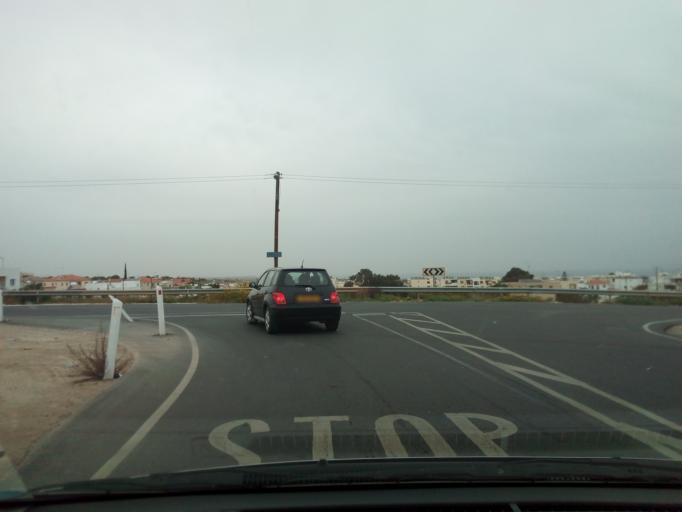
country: CY
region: Ammochostos
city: Paralimni
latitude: 35.0523
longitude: 33.9936
